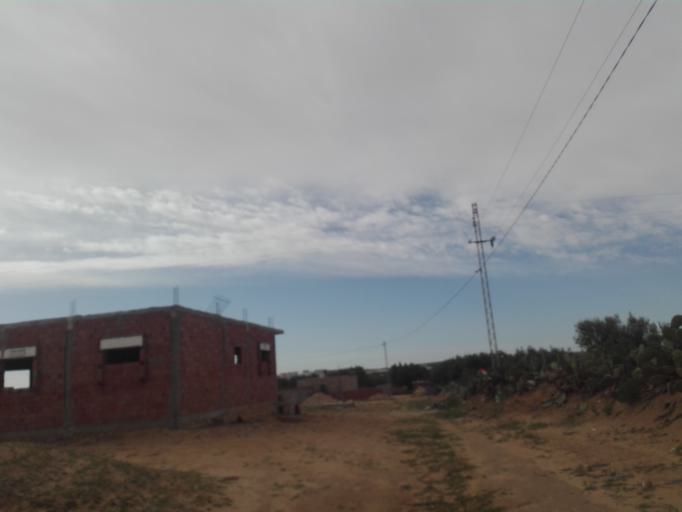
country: TN
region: Safaqis
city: Sfax
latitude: 34.7387
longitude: 10.5086
